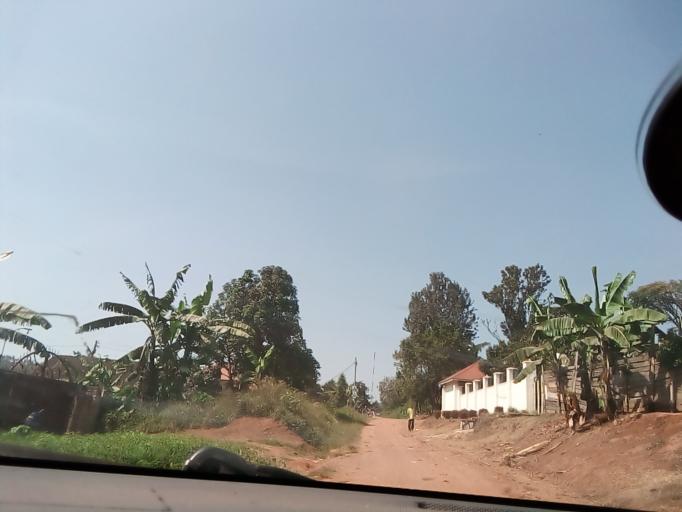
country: UG
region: Central Region
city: Masaka
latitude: -0.3499
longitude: 31.7435
